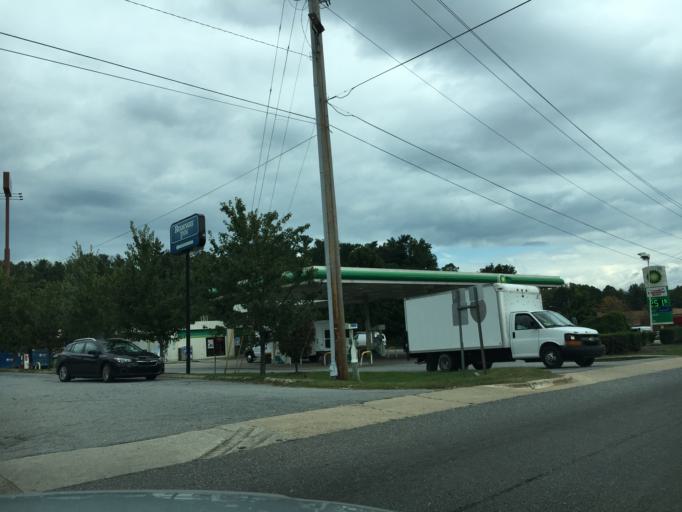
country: US
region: North Carolina
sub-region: Buncombe County
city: Bent Creek
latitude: 35.5604
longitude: -82.6364
